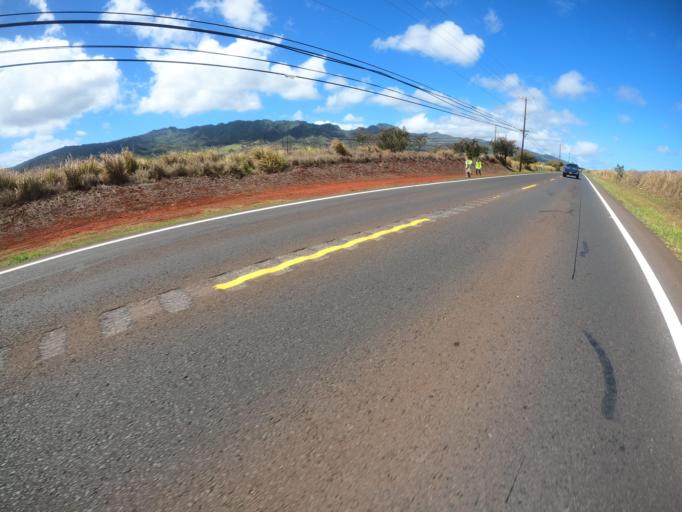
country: US
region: Hawaii
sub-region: Honolulu County
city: Village Park
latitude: 21.4109
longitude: -158.0445
